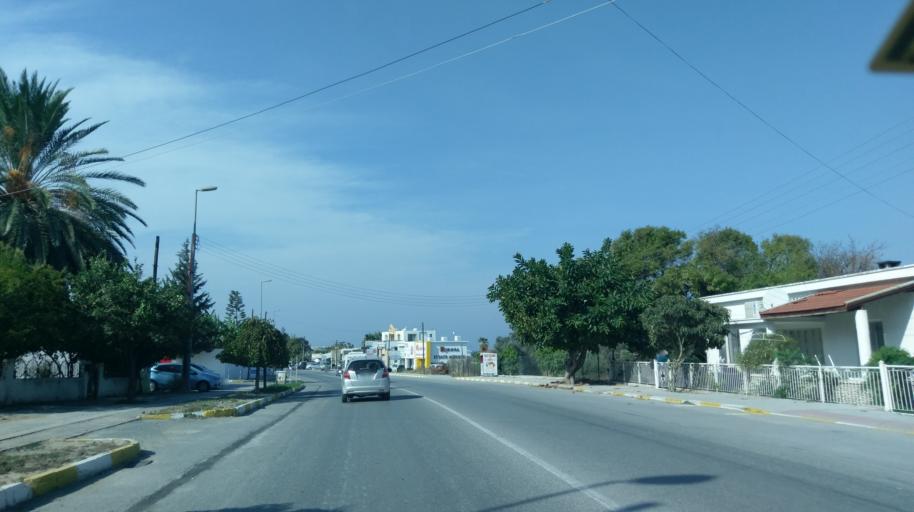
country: CY
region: Keryneia
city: Kyrenia
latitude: 35.3417
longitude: 33.2836
